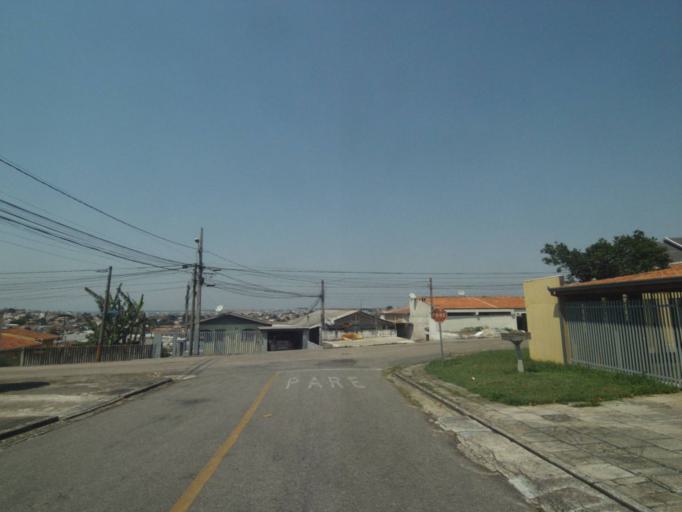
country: BR
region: Parana
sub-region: Sao Jose Dos Pinhais
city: Sao Jose dos Pinhais
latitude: -25.5086
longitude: -49.2723
